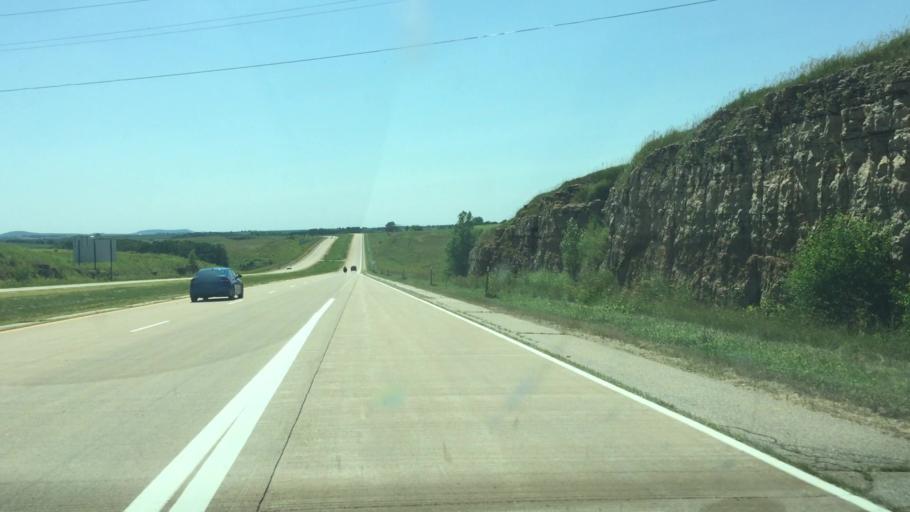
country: US
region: Wisconsin
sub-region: Iowa County
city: Mineral Point
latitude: 42.8843
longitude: -90.1719
